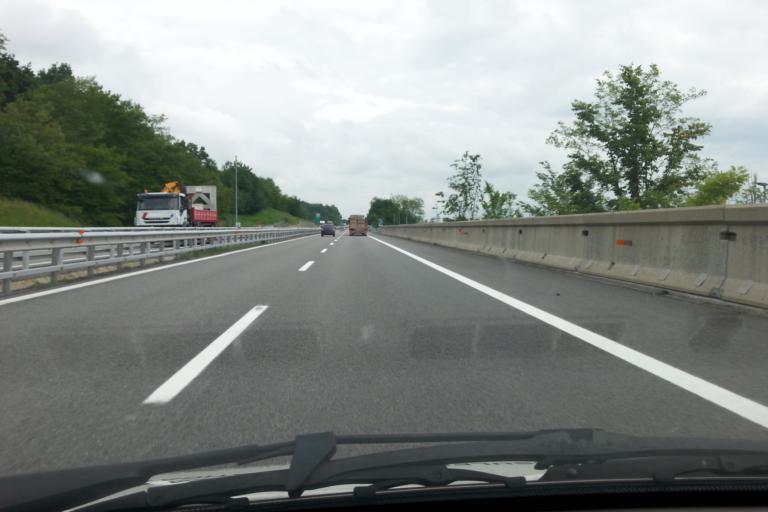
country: IT
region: Piedmont
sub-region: Provincia di Cuneo
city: Niella Tanaro
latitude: 44.4066
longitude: 7.9193
